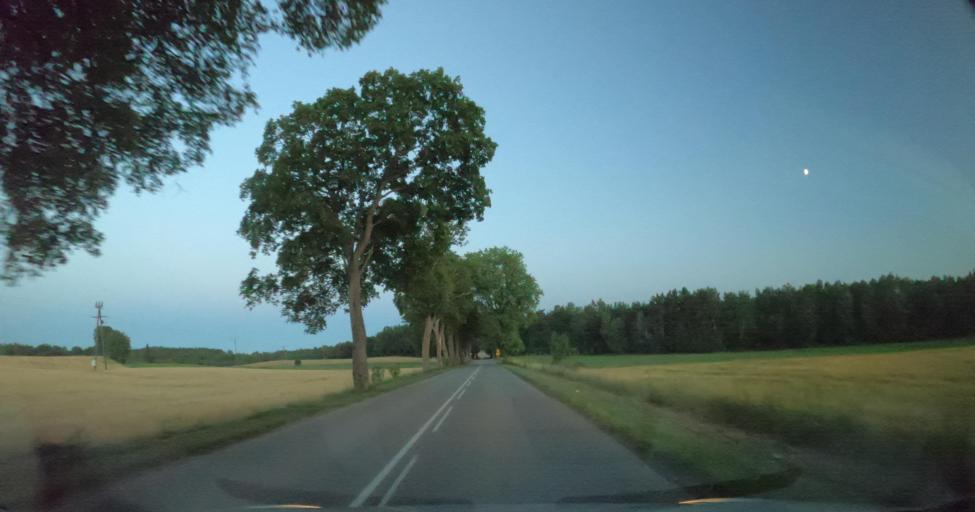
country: PL
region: Pomeranian Voivodeship
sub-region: Powiat wejherowski
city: Szemud
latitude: 54.4697
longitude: 18.2800
